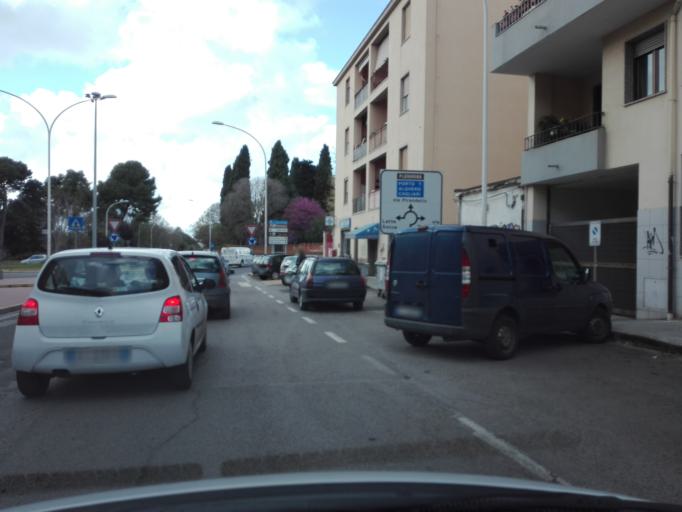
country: IT
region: Sardinia
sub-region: Provincia di Sassari
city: Sassari
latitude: 40.7368
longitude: 8.5608
